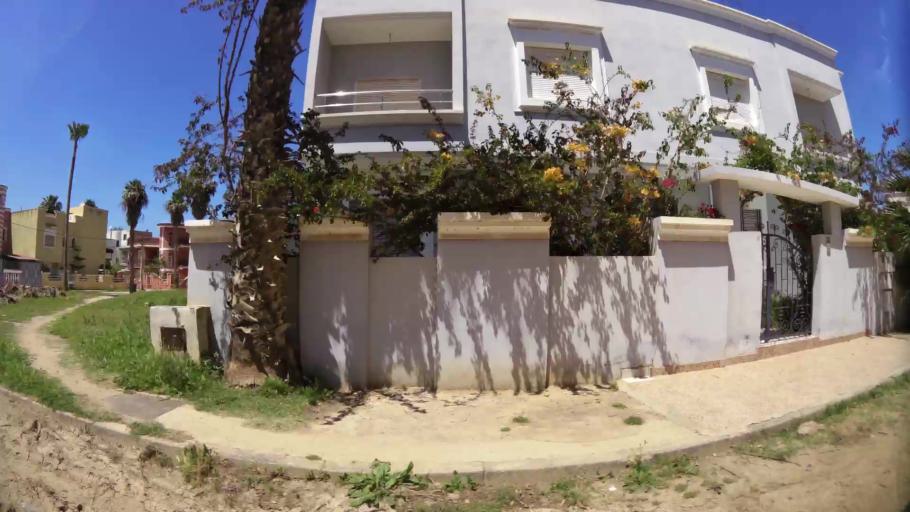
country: MA
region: Oriental
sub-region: Berkane-Taourirt
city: Madagh
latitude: 35.0731
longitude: -2.2174
